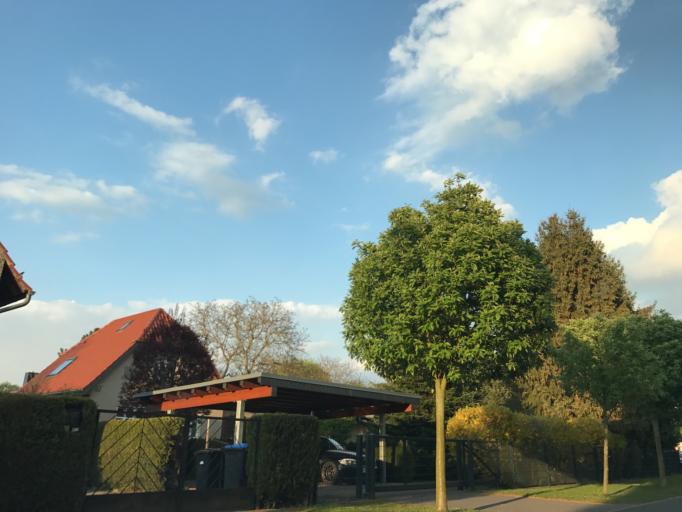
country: DE
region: Brandenburg
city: Falkensee
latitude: 52.5500
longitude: 13.0856
